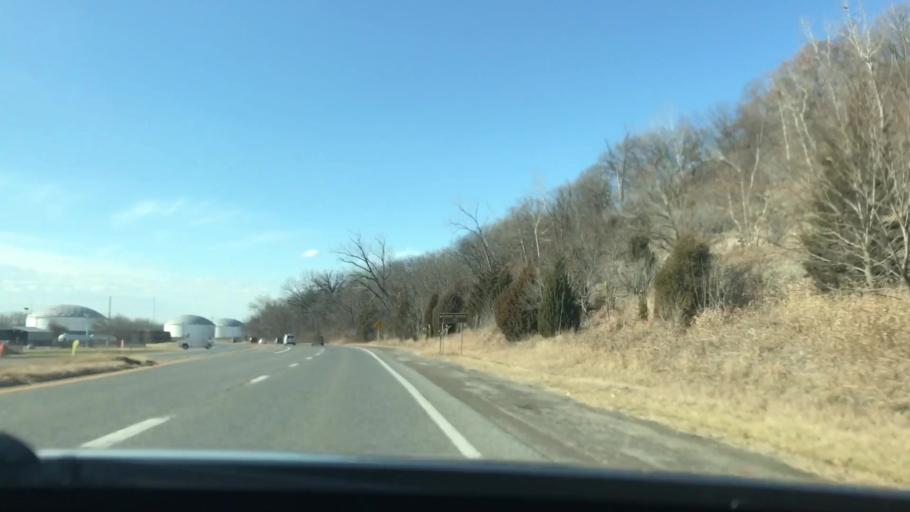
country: US
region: Missouri
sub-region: Platte County
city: Parkville
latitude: 39.1788
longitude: -94.6520
